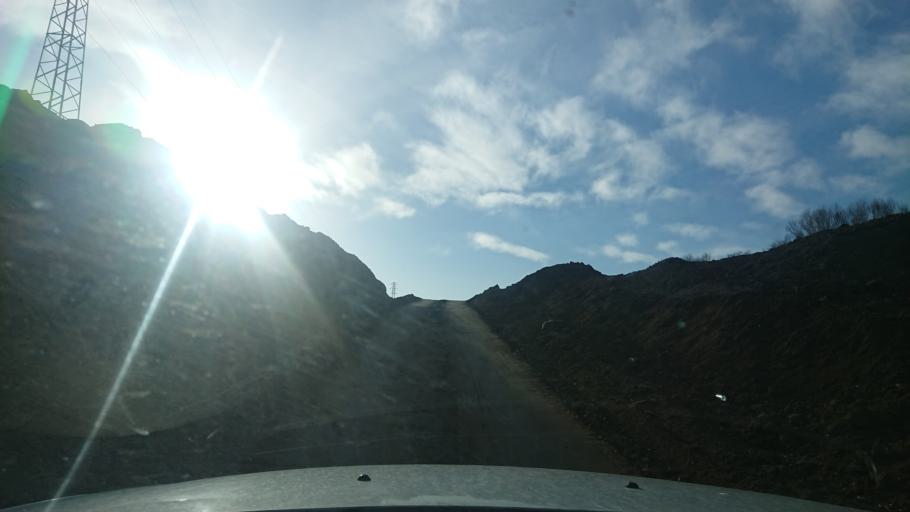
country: TR
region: Aksaray
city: Agacoren
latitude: 38.8609
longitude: 33.9417
